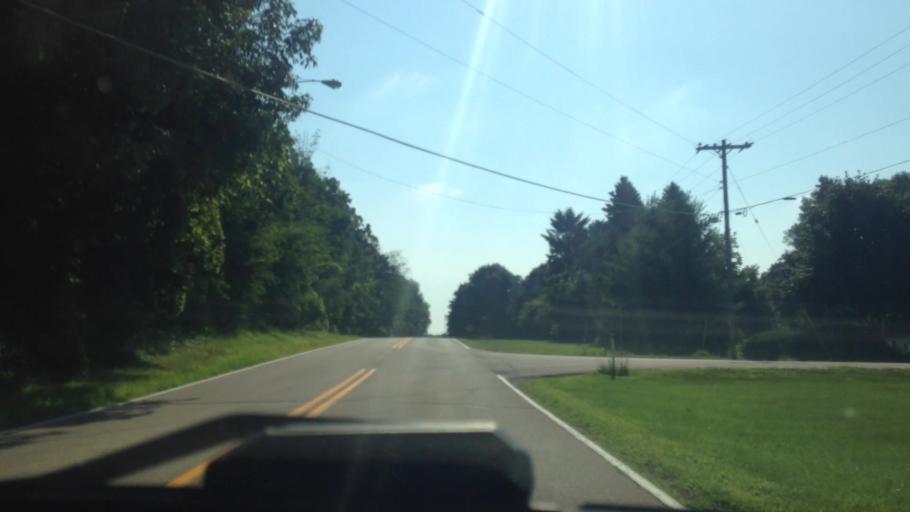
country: US
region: Wisconsin
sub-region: Waukesha County
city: Lannon
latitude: 43.1627
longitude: -88.1883
